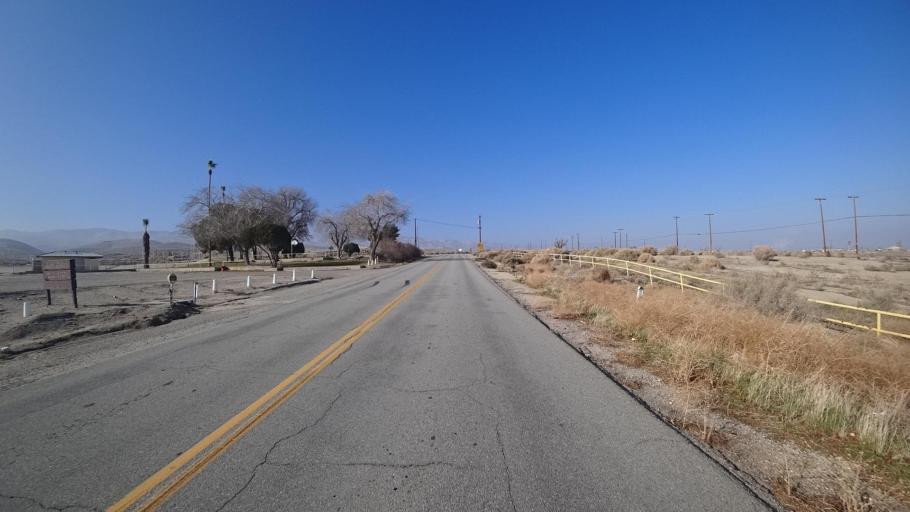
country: US
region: California
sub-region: Kern County
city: Taft Heights
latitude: 35.1794
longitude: -119.5472
